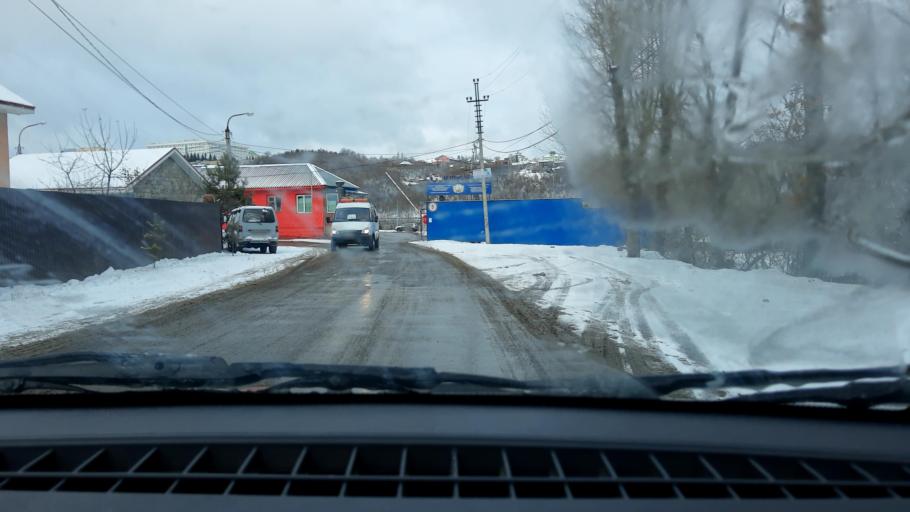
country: RU
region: Bashkortostan
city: Ufa
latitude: 54.7078
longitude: 55.9482
